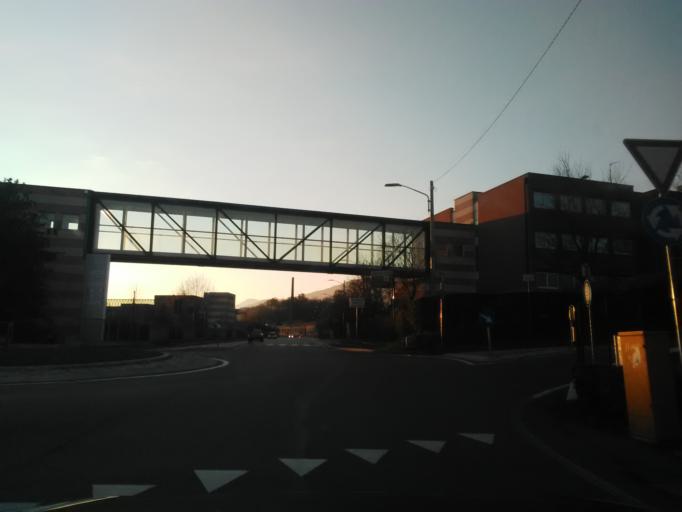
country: IT
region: Piedmont
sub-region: Provincia di Biella
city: Occhieppo Inferiore
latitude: 45.5571
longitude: 8.0344
